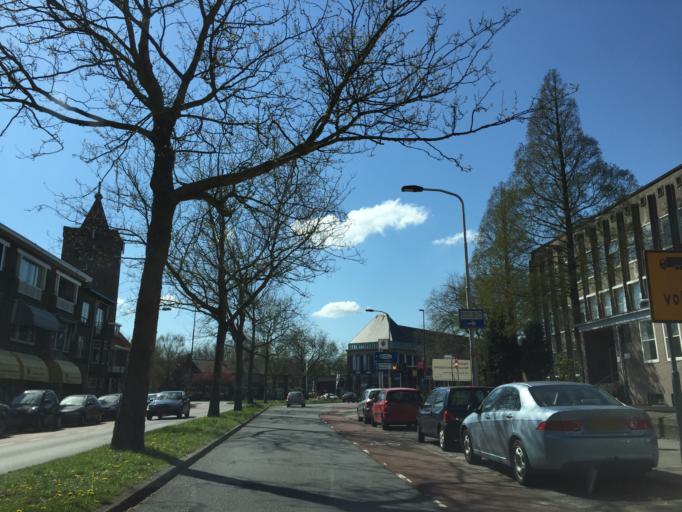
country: NL
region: South Holland
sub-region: Gemeente Delft
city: Delft
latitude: 52.0084
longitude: 4.3716
